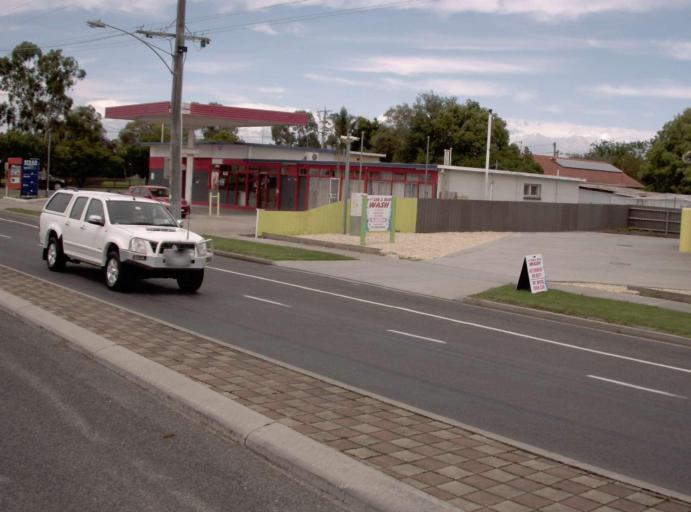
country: AU
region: Victoria
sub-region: Wellington
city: Sale
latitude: -37.9643
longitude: 147.0804
